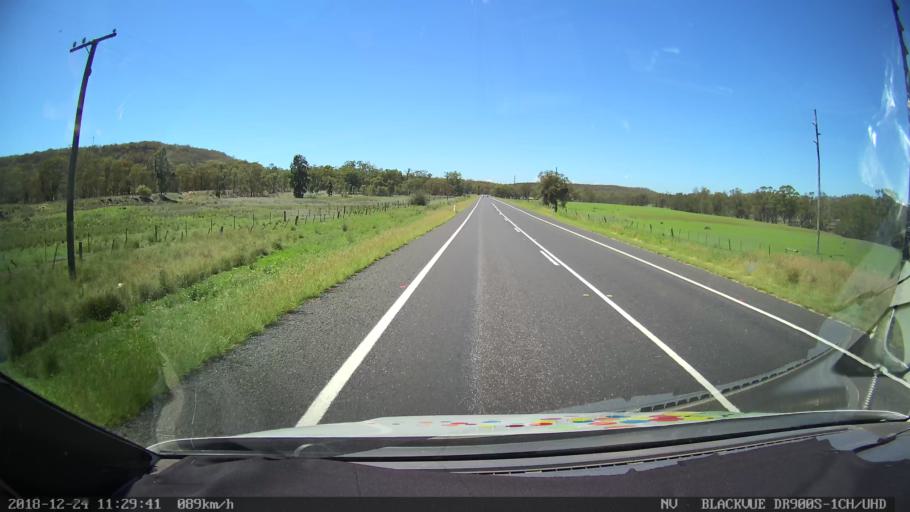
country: AU
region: New South Wales
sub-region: Upper Hunter Shire
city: Merriwa
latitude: -32.1955
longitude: 150.4643
